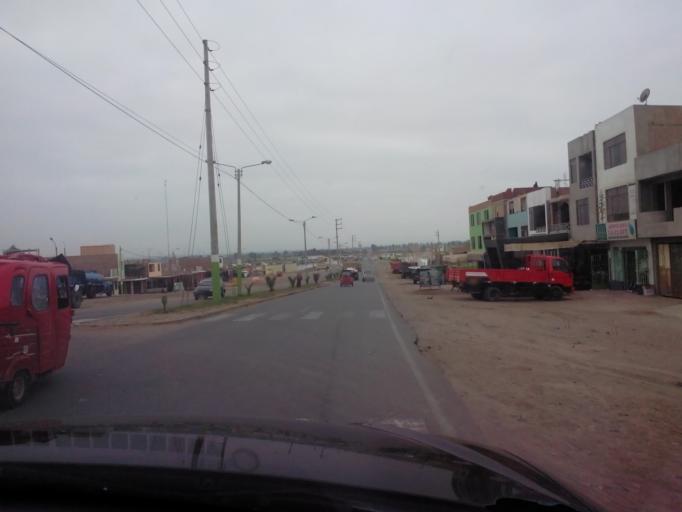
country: PE
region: Ica
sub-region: Provincia de Pisco
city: San Clemente
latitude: -13.6806
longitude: -76.1521
